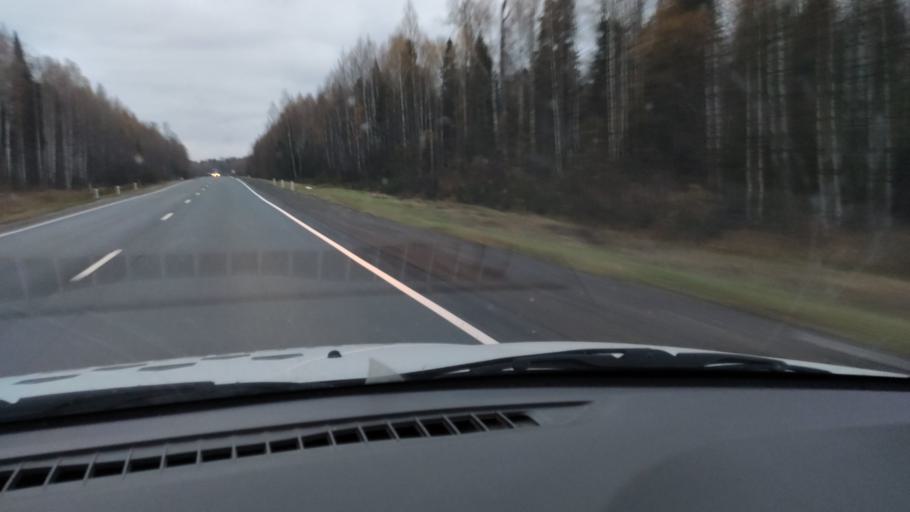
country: RU
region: Kirov
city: Kostino
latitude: 58.8375
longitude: 53.0561
